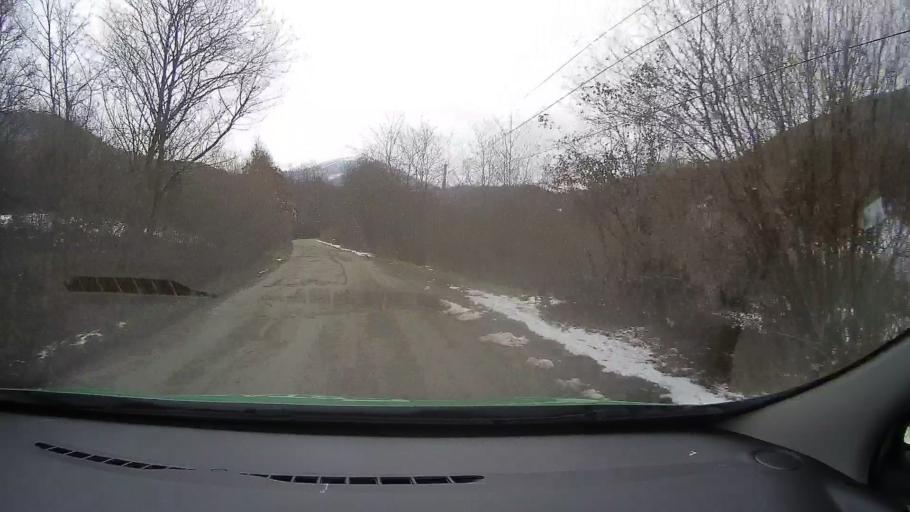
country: RO
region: Hunedoara
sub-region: Comuna Balsa
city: Balsa
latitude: 46.0218
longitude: 23.1254
